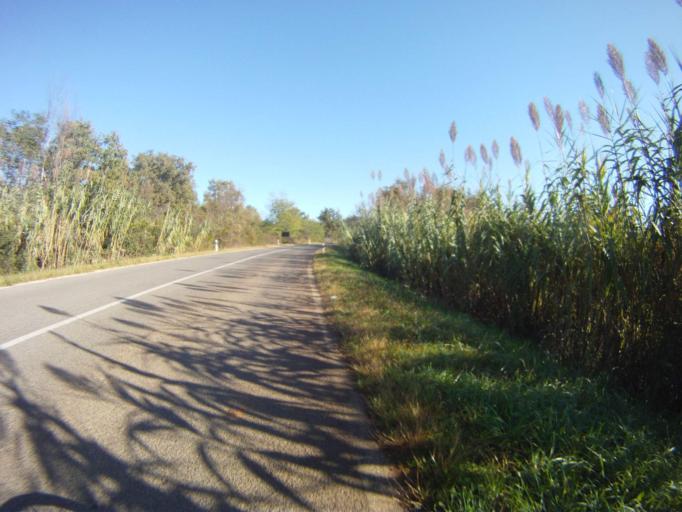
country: HR
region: Istarska
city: Buje
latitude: 45.3721
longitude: 13.6195
